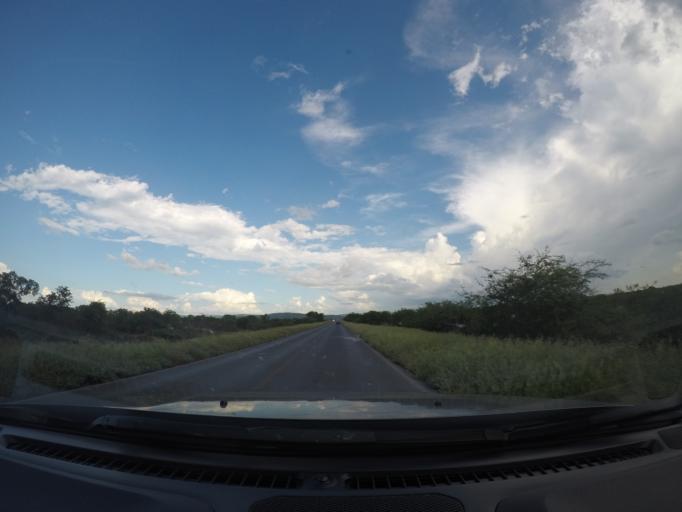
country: BR
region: Bahia
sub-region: Ibotirama
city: Ibotirama
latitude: -12.1760
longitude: -43.2502
